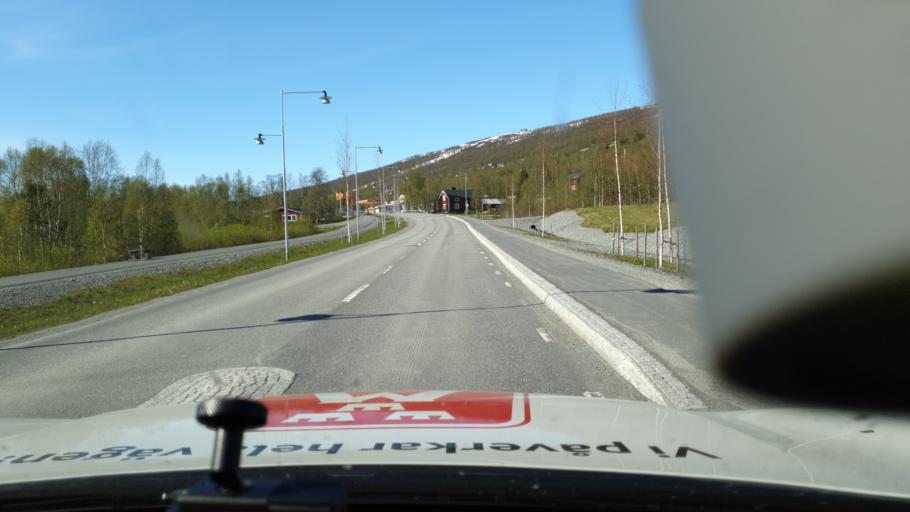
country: NO
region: Nordland
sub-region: Rana
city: Mo i Rana
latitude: 65.8159
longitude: 15.0875
